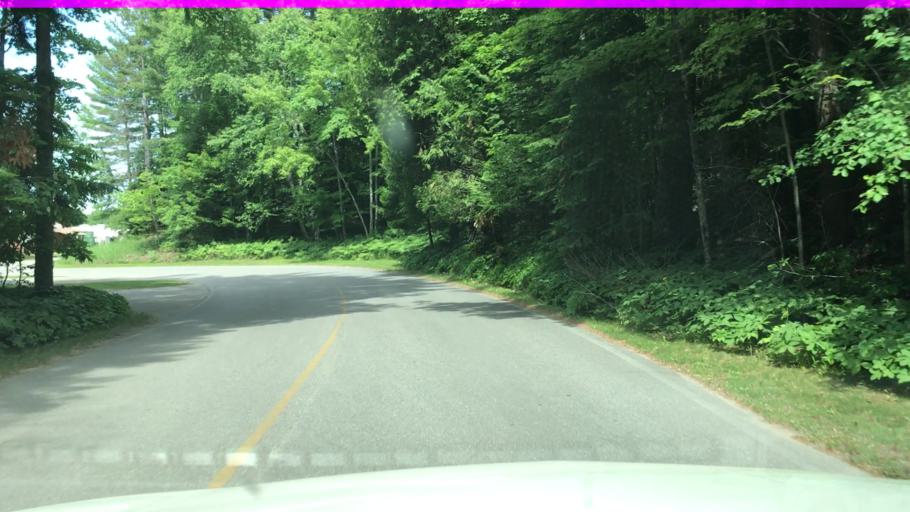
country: US
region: Michigan
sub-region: Schoolcraft County
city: Manistique
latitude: 45.9444
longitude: -86.3308
